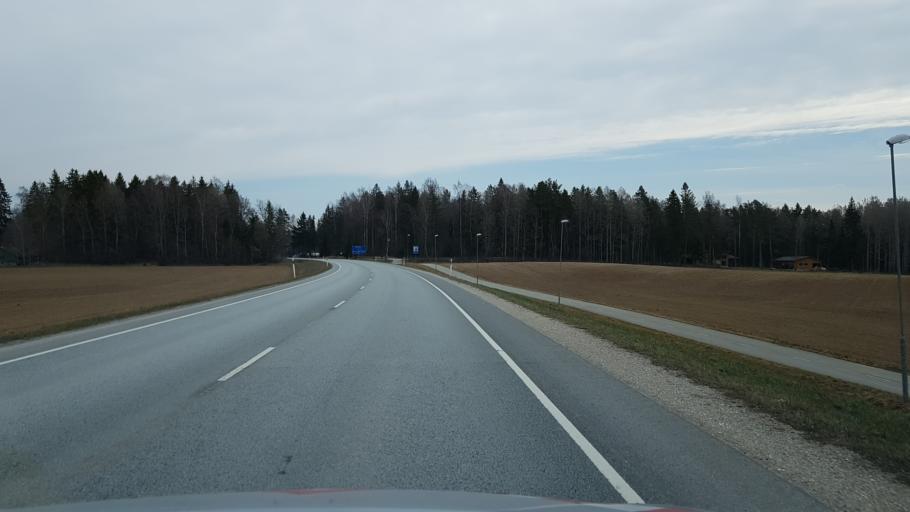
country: EE
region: Laeaene-Virumaa
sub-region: Rakvere linn
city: Rakvere
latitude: 59.3214
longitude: 26.3615
